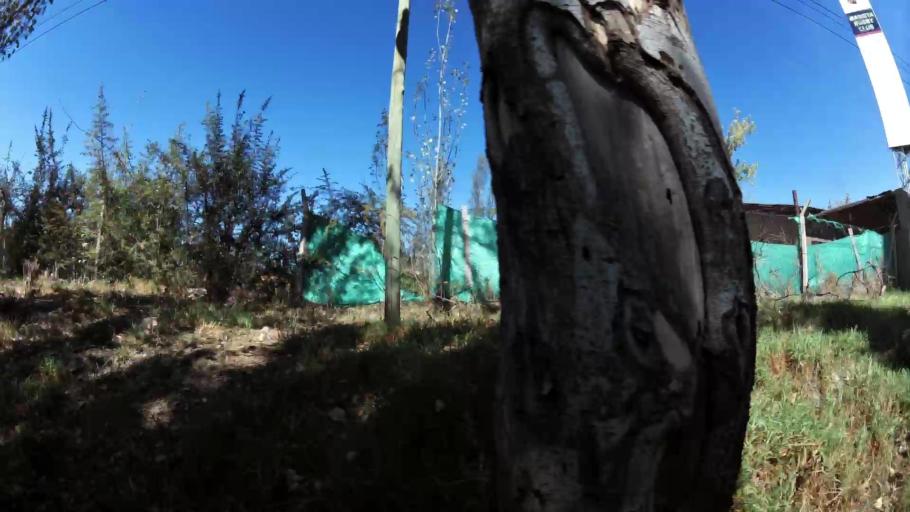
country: AR
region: Mendoza
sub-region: Departamento de Godoy Cruz
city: Godoy Cruz
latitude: -32.9770
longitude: -68.8409
